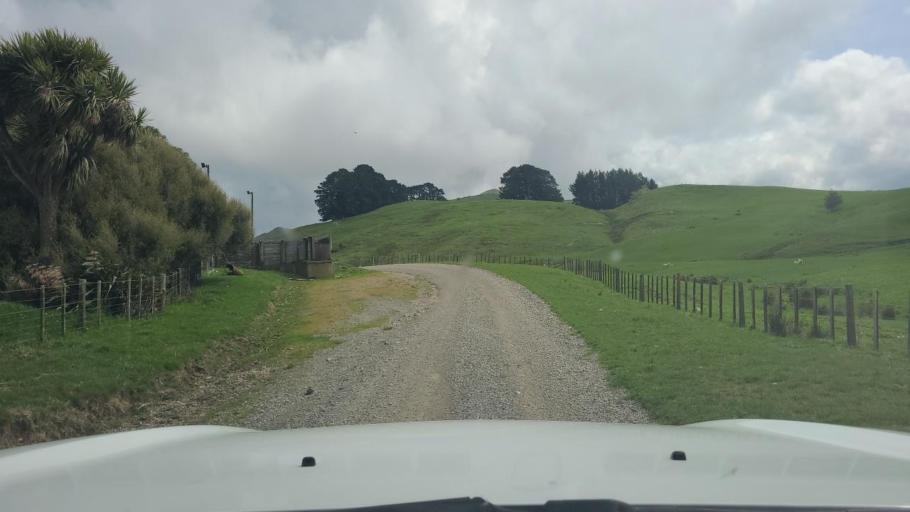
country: NZ
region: Wellington
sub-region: Masterton District
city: Masterton
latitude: -40.9232
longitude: 175.5389
